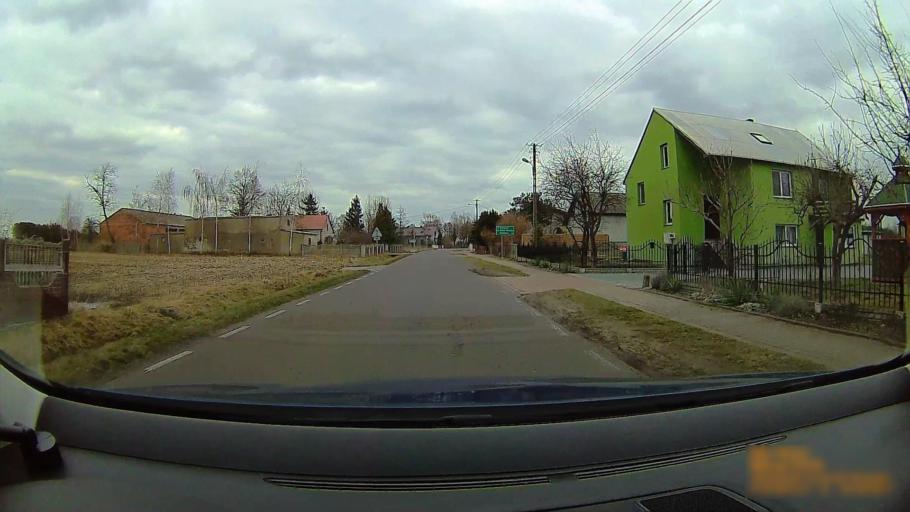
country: PL
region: Greater Poland Voivodeship
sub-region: Powiat koninski
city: Rzgow Pierwszy
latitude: 52.1043
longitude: 18.0888
